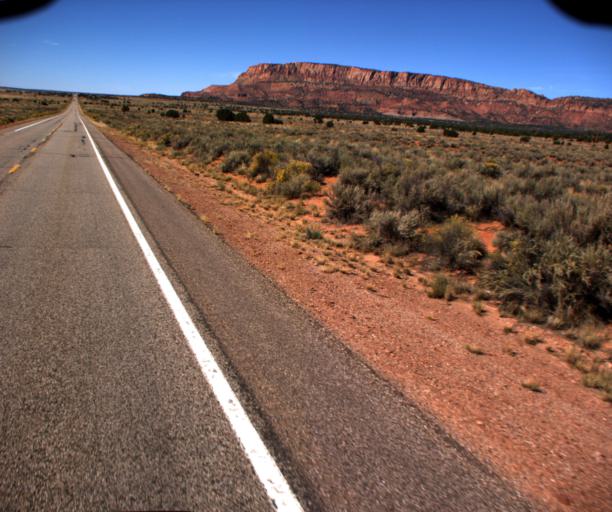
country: US
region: Arizona
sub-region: Coconino County
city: Fredonia
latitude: 36.8577
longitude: -112.7435
